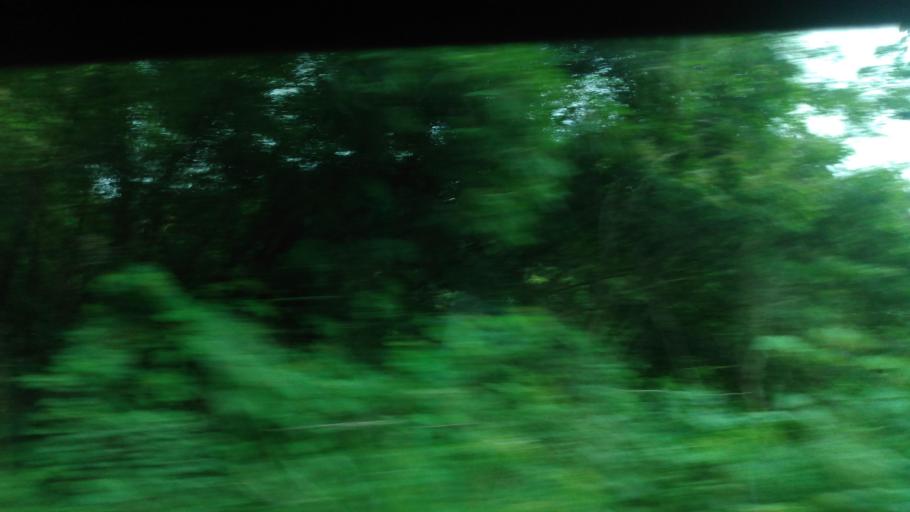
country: BR
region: Pernambuco
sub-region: Maraial
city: Maraial
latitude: -8.7837
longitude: -35.9085
